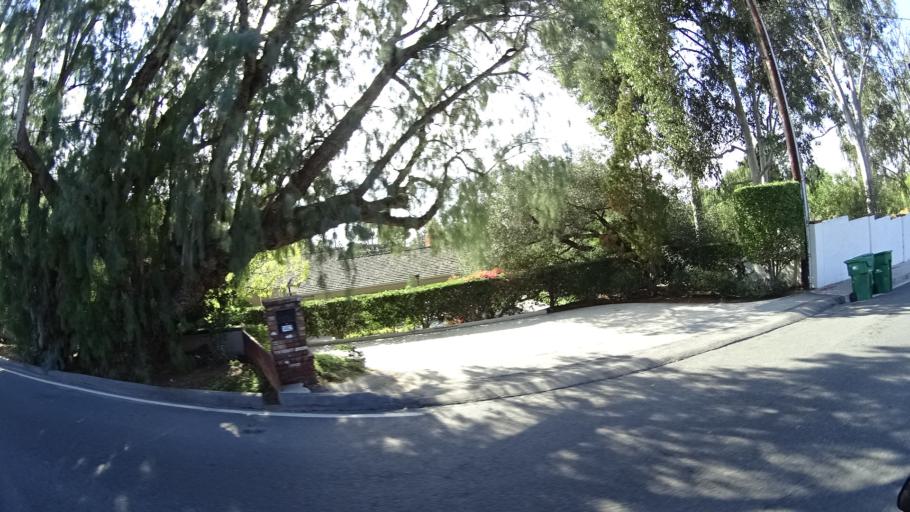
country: US
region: California
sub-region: Orange County
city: North Tustin
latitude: 33.7617
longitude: -117.7880
